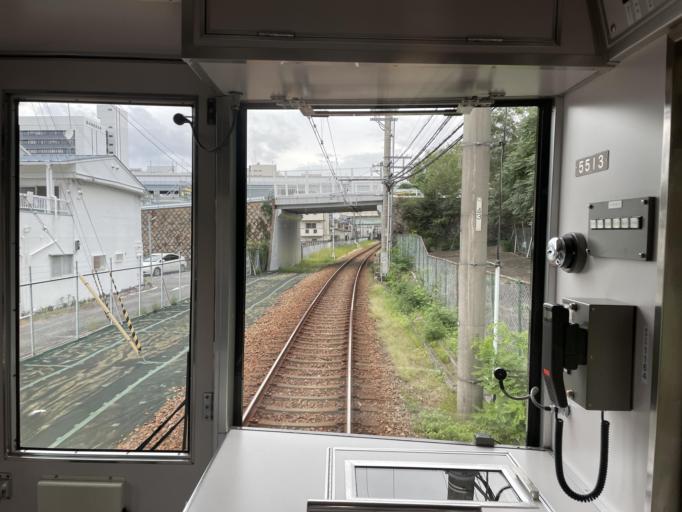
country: JP
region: Hyogo
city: Amagasaki
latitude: 34.7150
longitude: 135.3796
